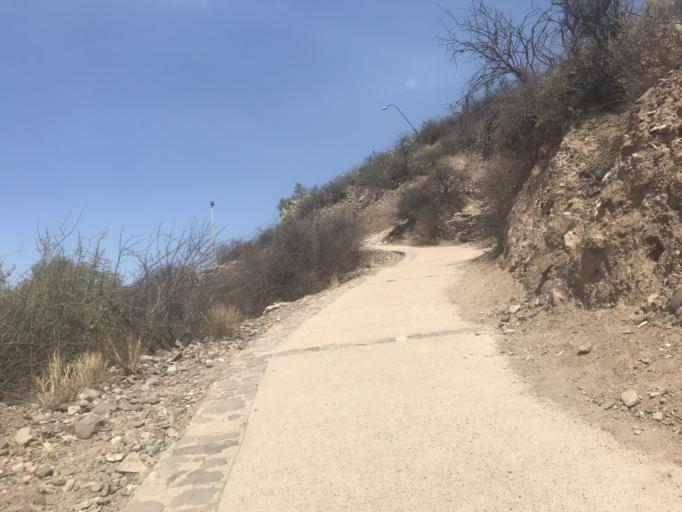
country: AR
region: Mendoza
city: Mendoza
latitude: -32.8850
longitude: -68.8897
